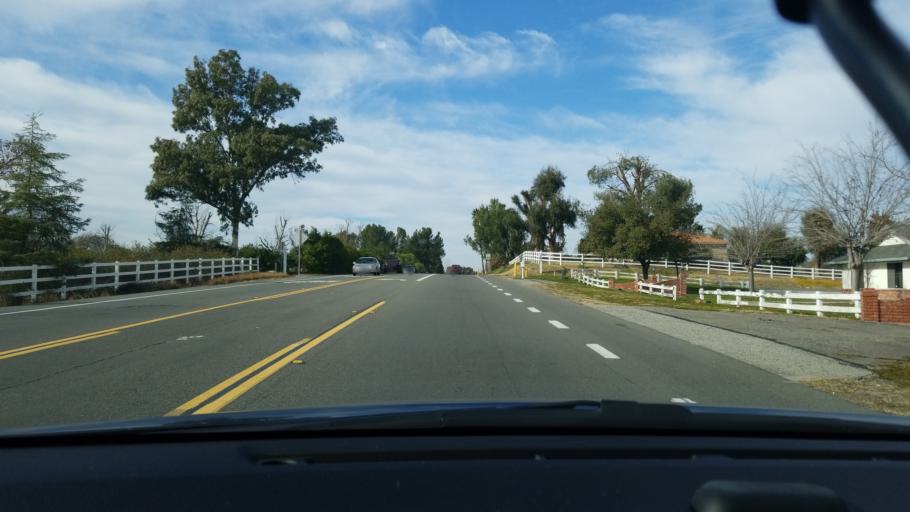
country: US
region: California
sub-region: Riverside County
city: Temecula
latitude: 33.4820
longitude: -117.1332
